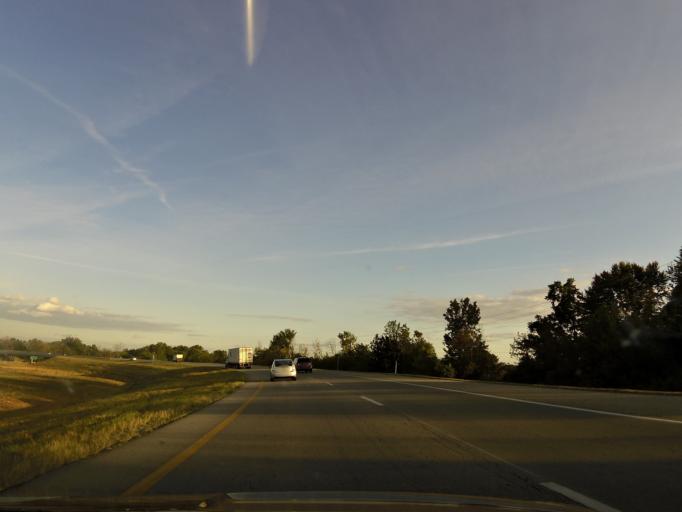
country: US
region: Indiana
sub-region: Boone County
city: Whitestown
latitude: 39.9331
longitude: -86.3432
